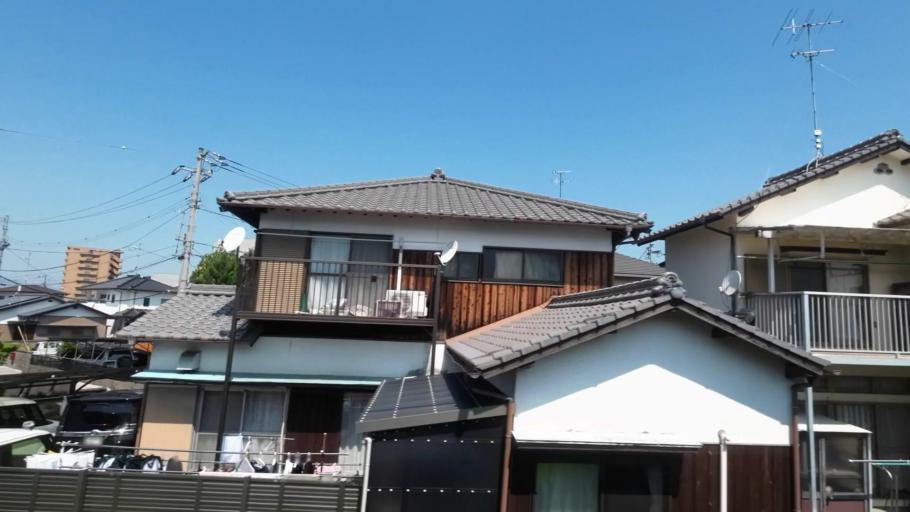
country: JP
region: Ehime
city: Saijo
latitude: 33.9105
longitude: 133.1836
